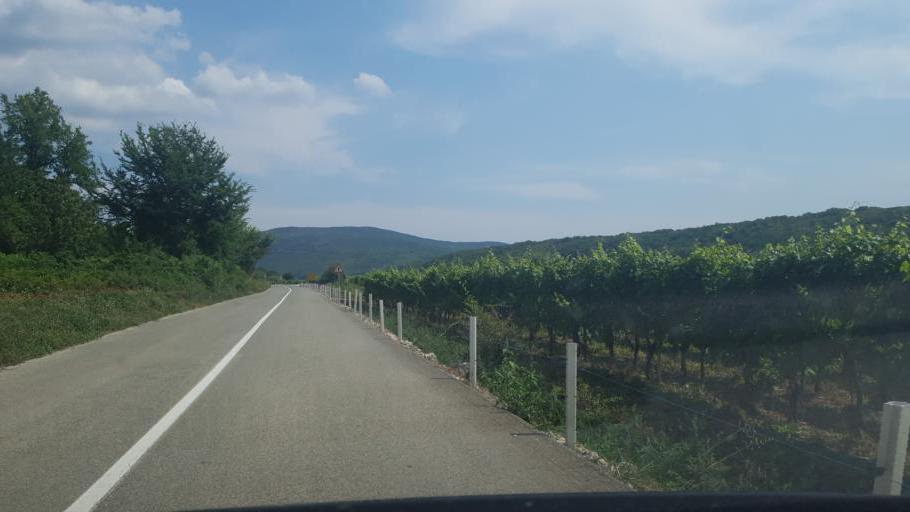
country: HR
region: Primorsko-Goranska
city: Punat
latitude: 45.0845
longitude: 14.6460
